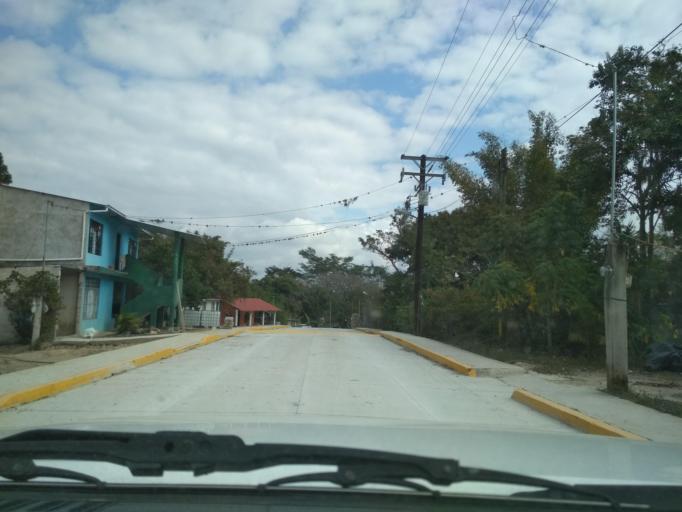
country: MX
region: Veracruz
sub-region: Coatepec
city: Tuzamapan
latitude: 19.3692
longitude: -96.8792
